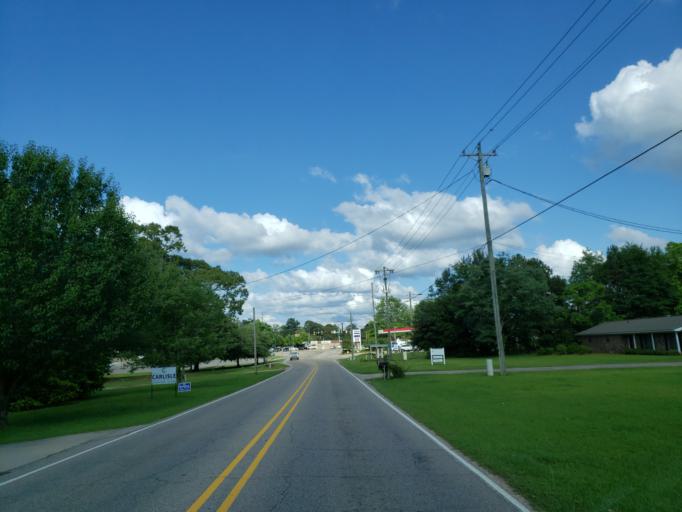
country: US
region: Mississippi
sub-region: Lamar County
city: West Hattiesburg
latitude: 31.2862
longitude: -89.4165
